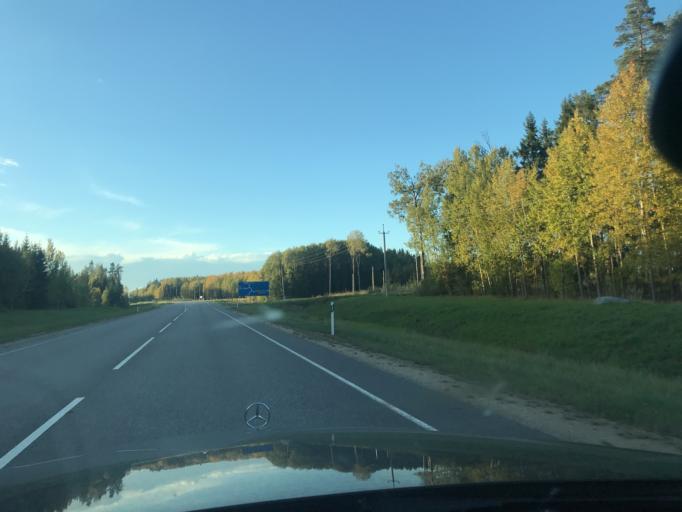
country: EE
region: Vorumaa
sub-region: Voru linn
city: Voru
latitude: 57.8465
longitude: 27.0432
